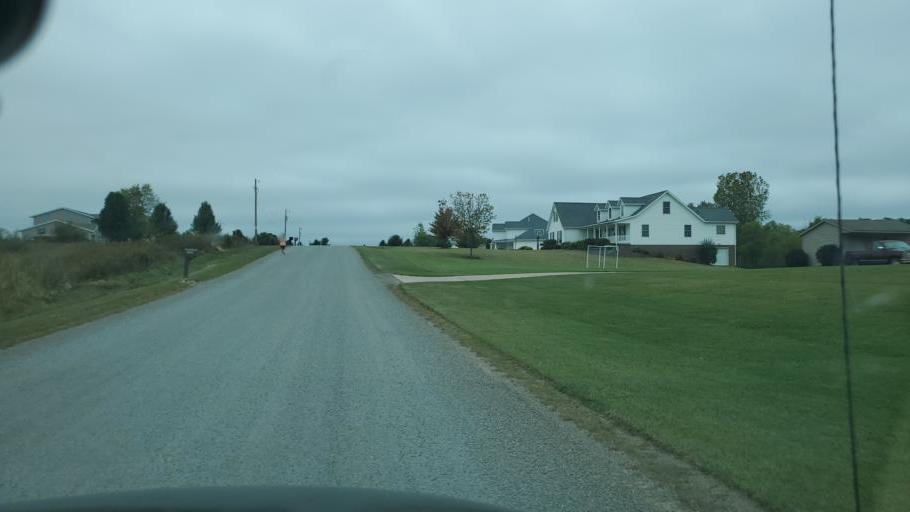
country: US
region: Ohio
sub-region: Richland County
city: Lexington
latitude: 40.6602
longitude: -82.6204
